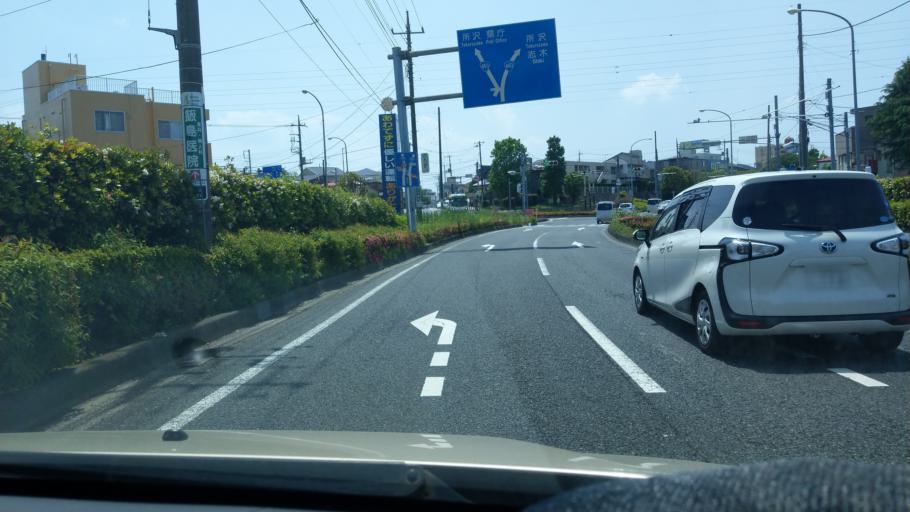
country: JP
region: Saitama
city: Yono
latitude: 35.8682
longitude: 139.6643
